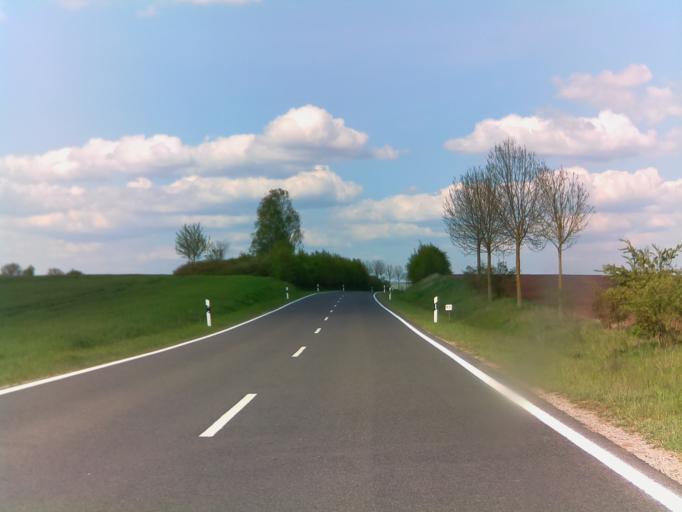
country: DE
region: Thuringia
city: Gleichamberg
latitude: 50.3542
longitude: 10.6205
